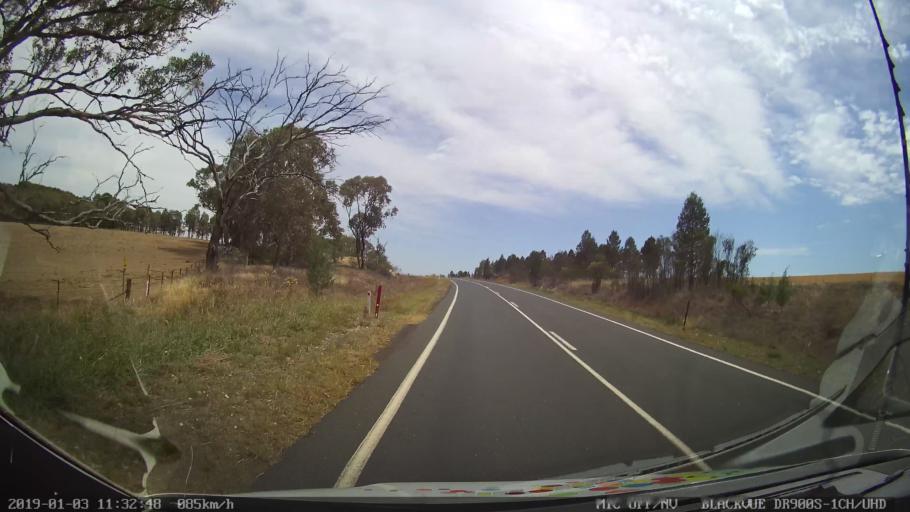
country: AU
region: New South Wales
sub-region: Weddin
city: Grenfell
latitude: -33.9538
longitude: 148.1765
